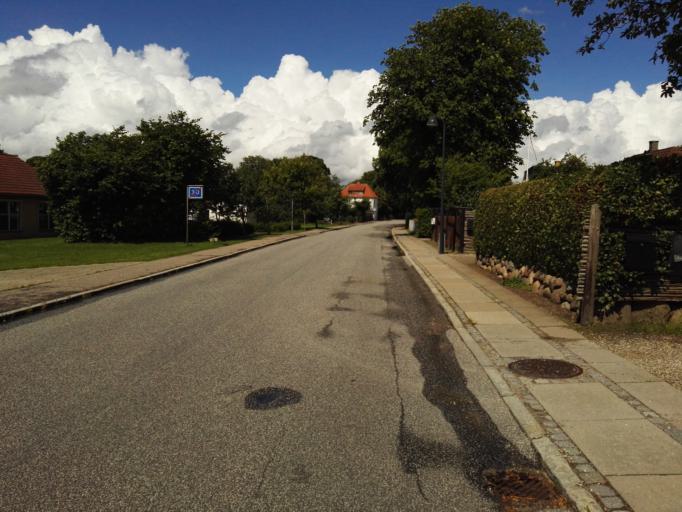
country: DK
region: Capital Region
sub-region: Egedal Kommune
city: Vekso
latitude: 55.7529
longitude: 12.2388
